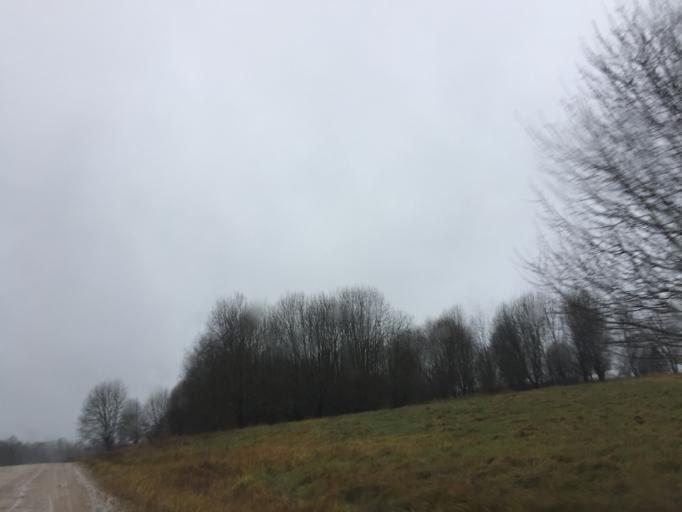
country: LV
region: Salas
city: Sala
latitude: 56.4934
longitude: 25.6817
